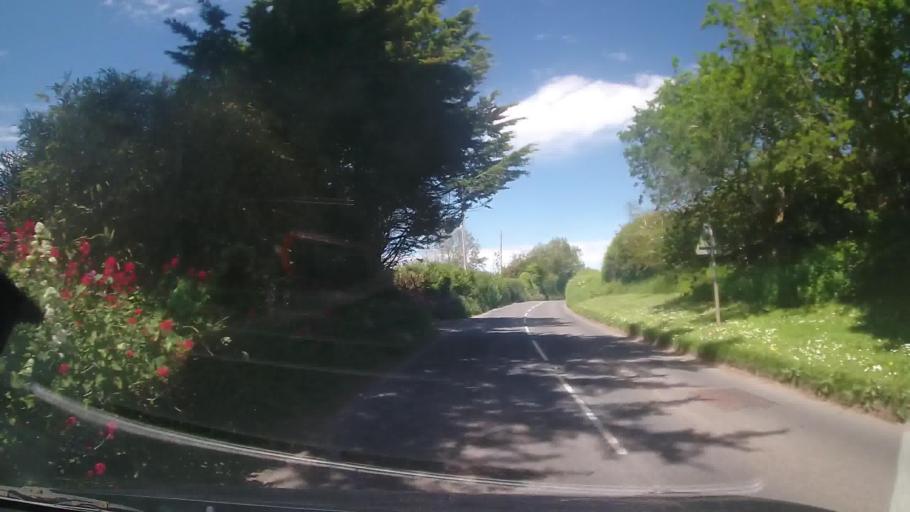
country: GB
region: England
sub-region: Devon
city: Kingsbridge
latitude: 50.2695
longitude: -3.7568
